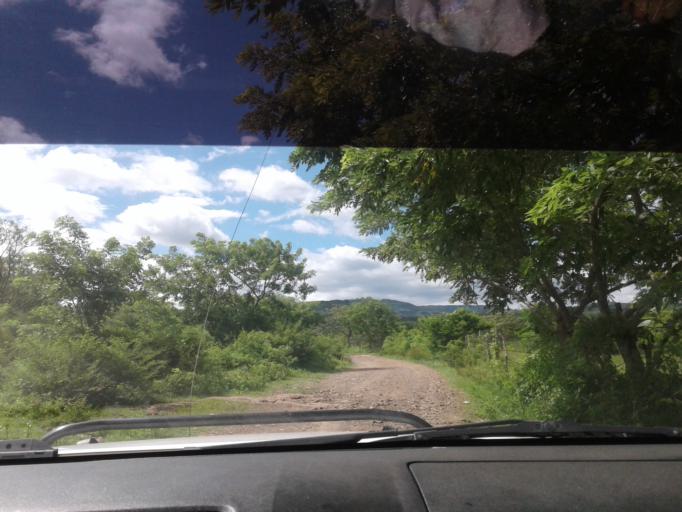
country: NI
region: Matagalpa
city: Ciudad Dario
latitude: 12.8461
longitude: -86.2194
